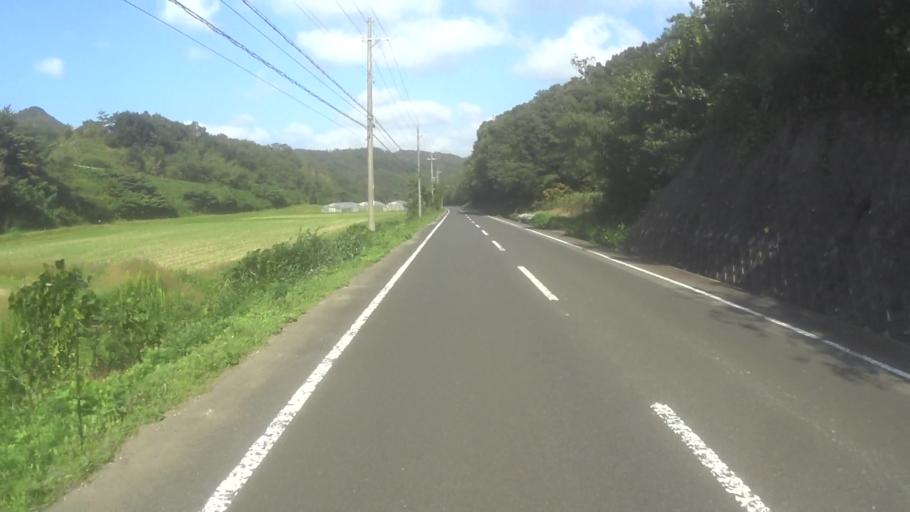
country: JP
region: Kyoto
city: Miyazu
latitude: 35.7051
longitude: 135.0765
